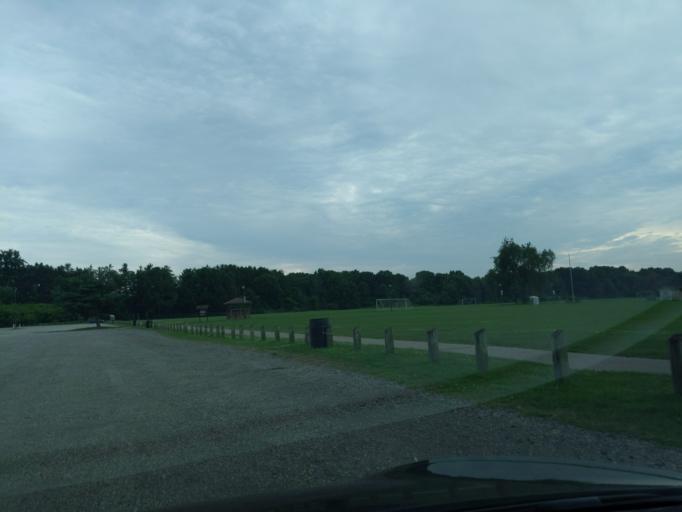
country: US
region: Michigan
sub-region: Livingston County
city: Whitmore Lake
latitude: 42.4487
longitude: -83.8224
